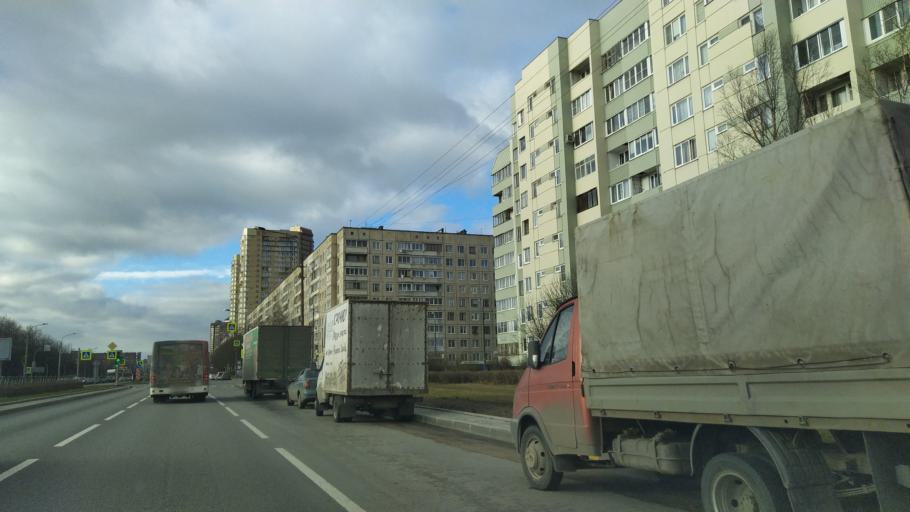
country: RU
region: Leningrad
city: Akademicheskoe
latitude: 60.0332
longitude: 30.3810
